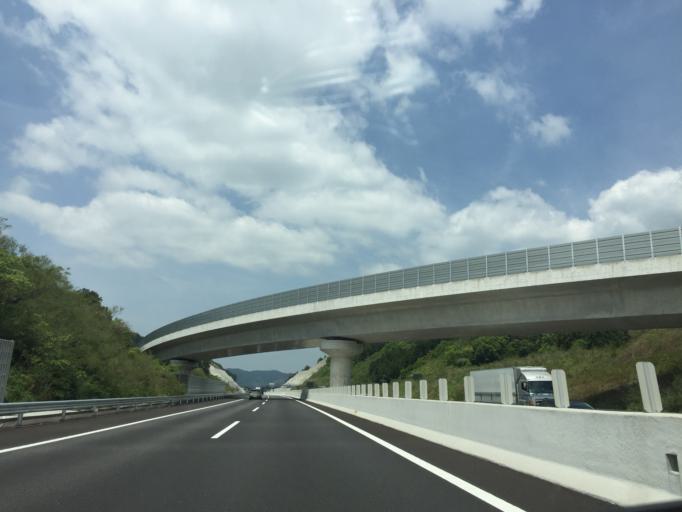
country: JP
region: Aichi
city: Shinshiro
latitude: 34.8894
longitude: 137.6469
